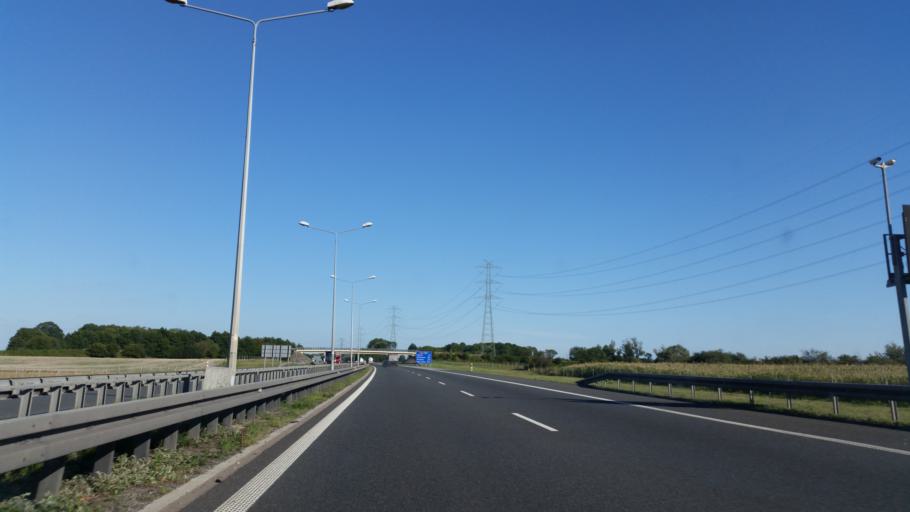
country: PL
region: Opole Voivodeship
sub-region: Powiat brzeski
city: Grodkow
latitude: 50.7792
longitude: 17.3539
